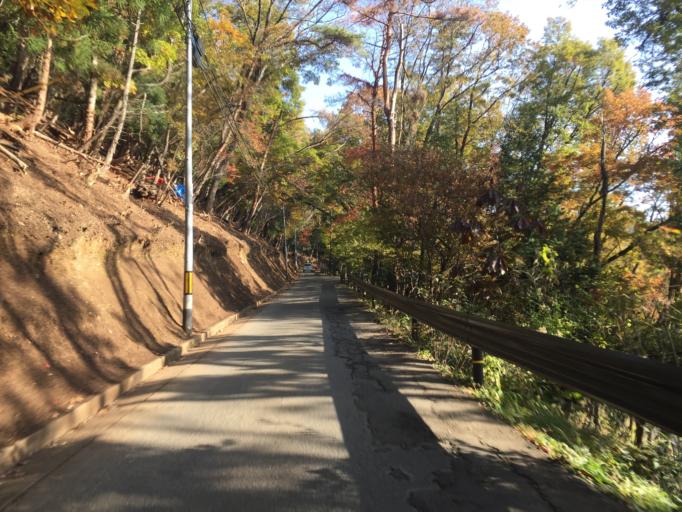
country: JP
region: Fukushima
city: Fukushima-shi
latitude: 37.7713
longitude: 140.4702
